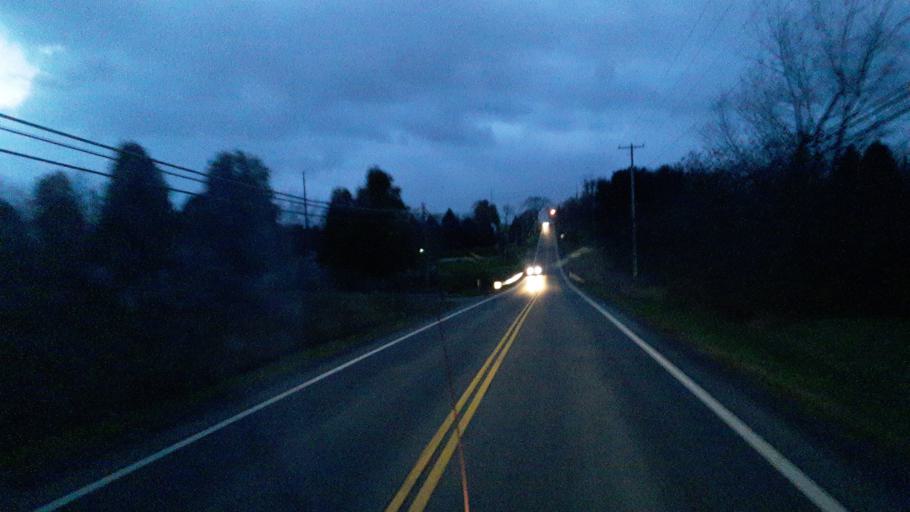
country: US
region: Ohio
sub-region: Portage County
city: Streetsboro
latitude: 41.2387
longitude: -81.3091
